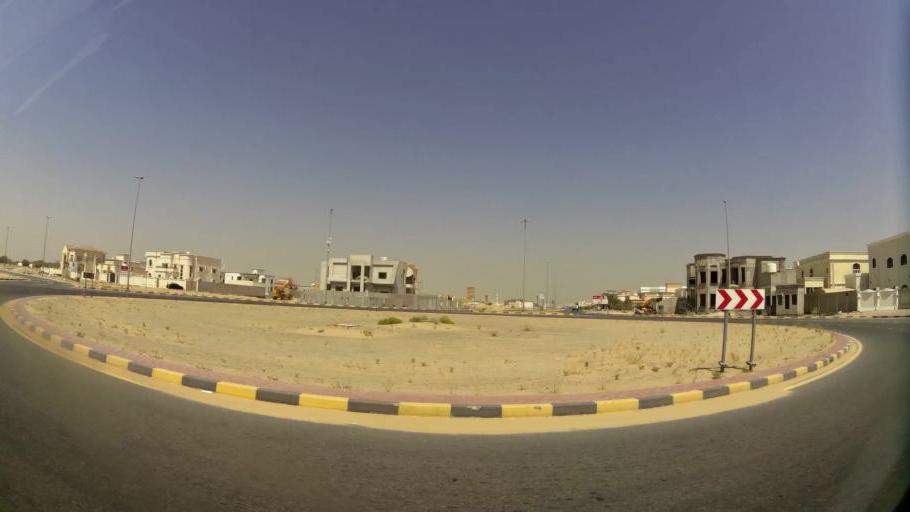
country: AE
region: Ajman
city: Ajman
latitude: 25.4049
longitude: 55.5392
